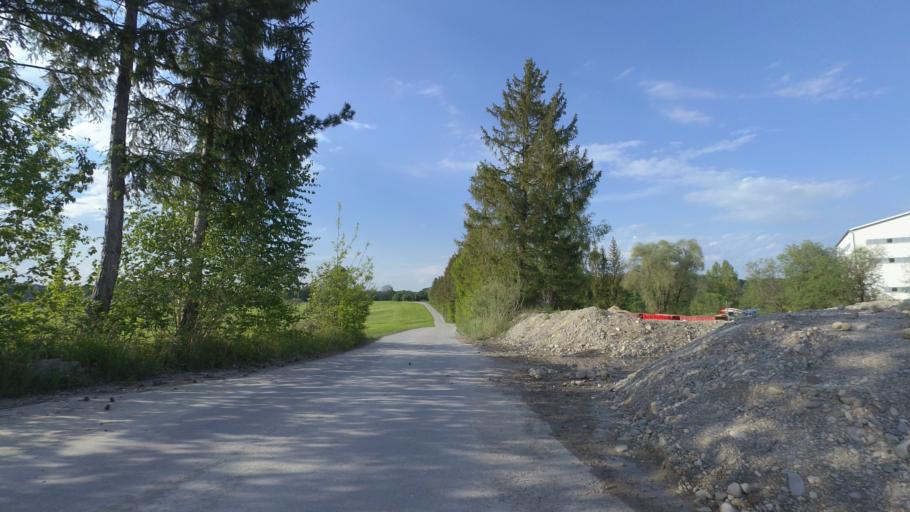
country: DE
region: Bavaria
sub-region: Upper Bavaria
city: Chieming
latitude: 47.8951
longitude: 12.5675
